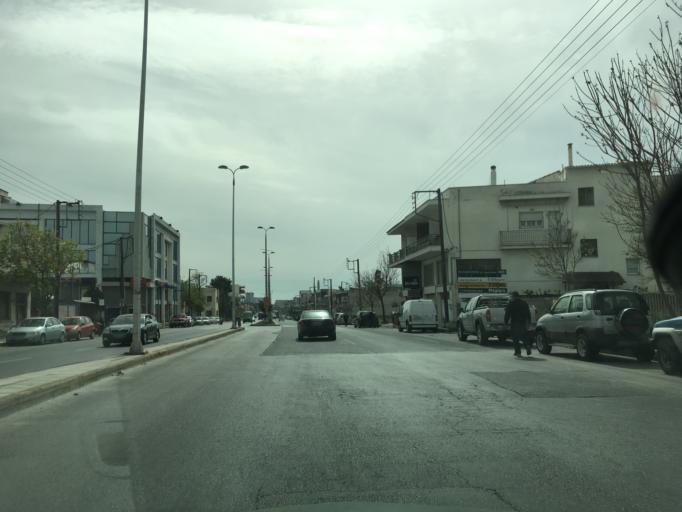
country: GR
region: Thessaly
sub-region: Nomos Magnisias
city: Nea Ionia
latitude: 39.3658
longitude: 22.9248
